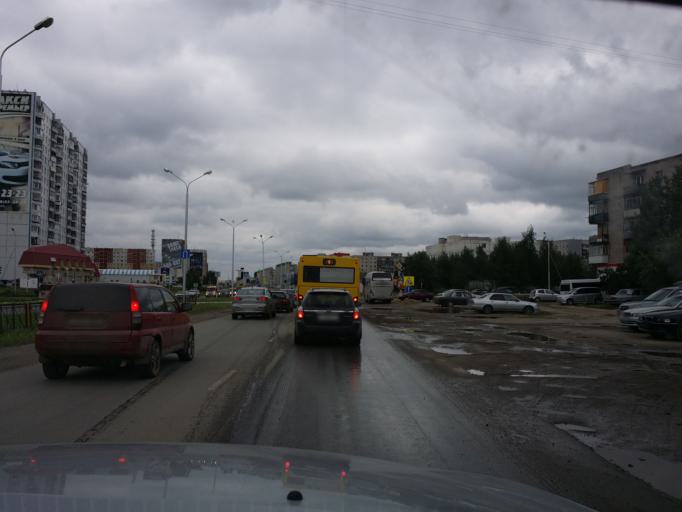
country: RU
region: Khanty-Mansiyskiy Avtonomnyy Okrug
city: Nizhnevartovsk
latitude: 60.9471
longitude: 76.5952
